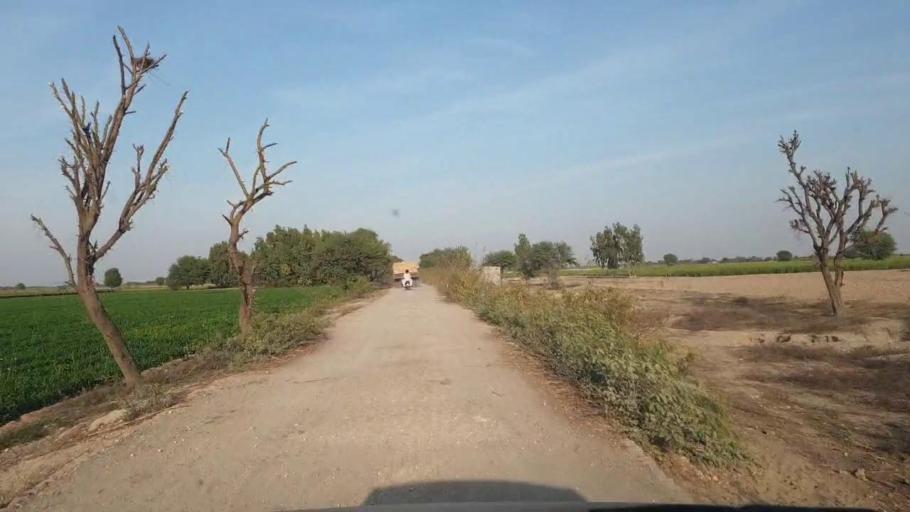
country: PK
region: Sindh
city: Chambar
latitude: 25.2381
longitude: 68.7912
